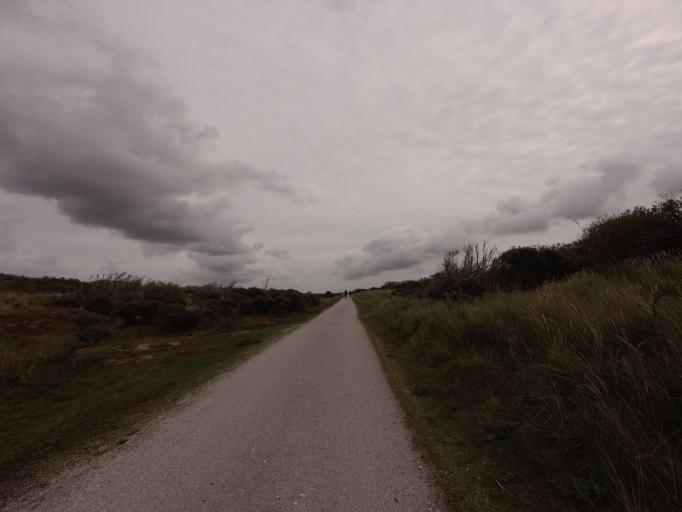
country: NL
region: Friesland
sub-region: Gemeente Ameland
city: Hollum
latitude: 53.4582
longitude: 5.6799
